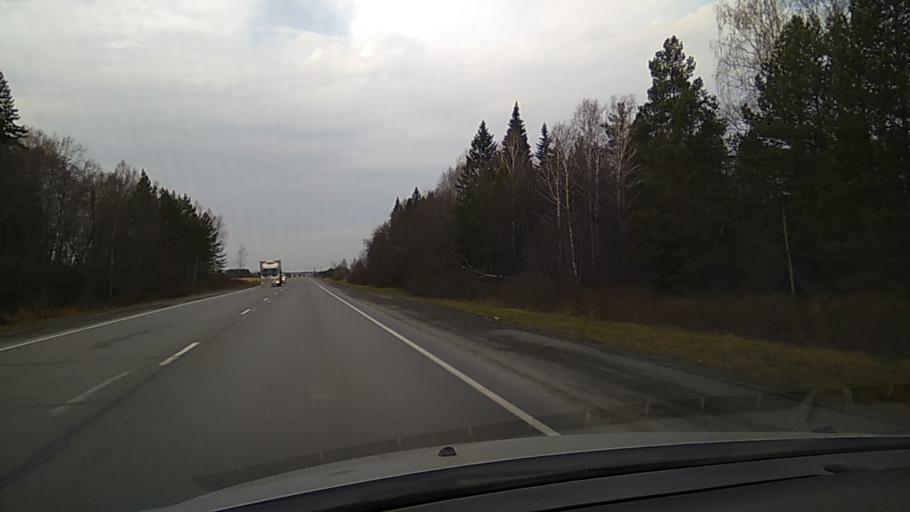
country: RU
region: Sverdlovsk
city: Tugulym
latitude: 57.0725
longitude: 64.5956
